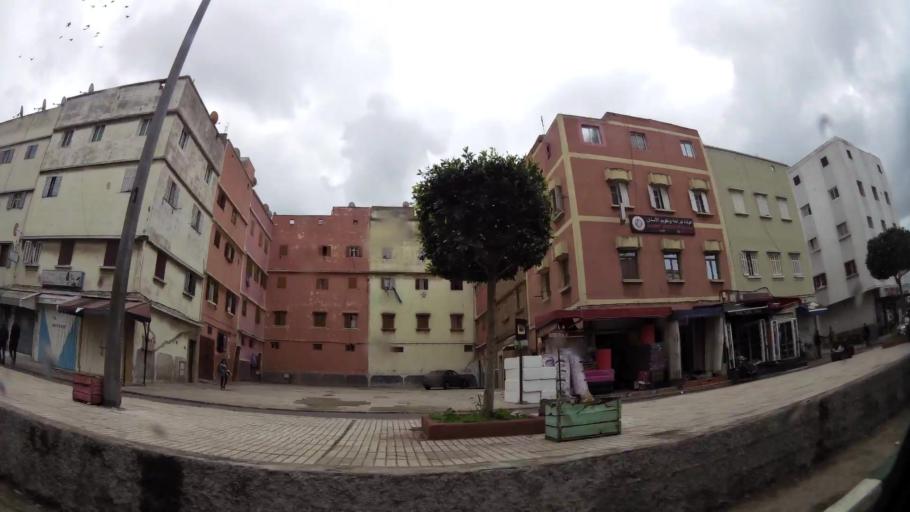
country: MA
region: Grand Casablanca
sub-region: Mediouna
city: Tit Mellil
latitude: 33.6054
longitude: -7.5088
